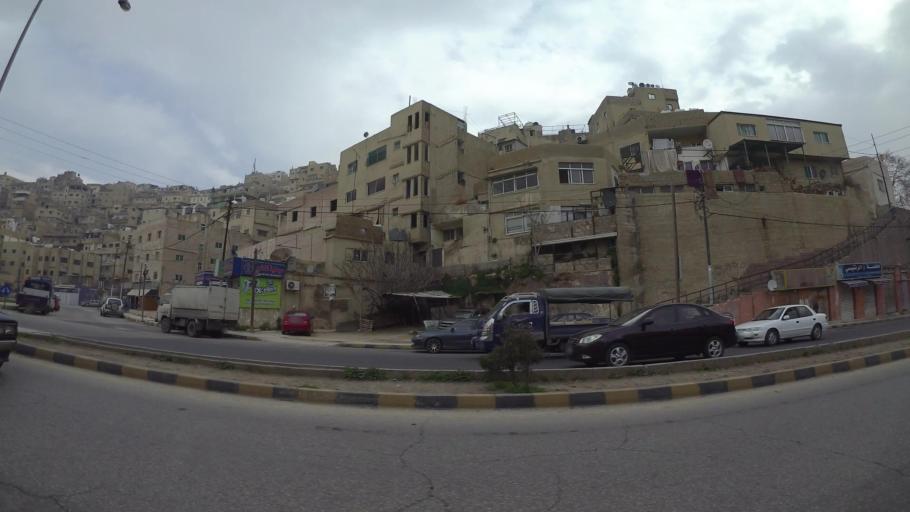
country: JO
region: Amman
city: Amman
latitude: 31.9565
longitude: 35.9373
